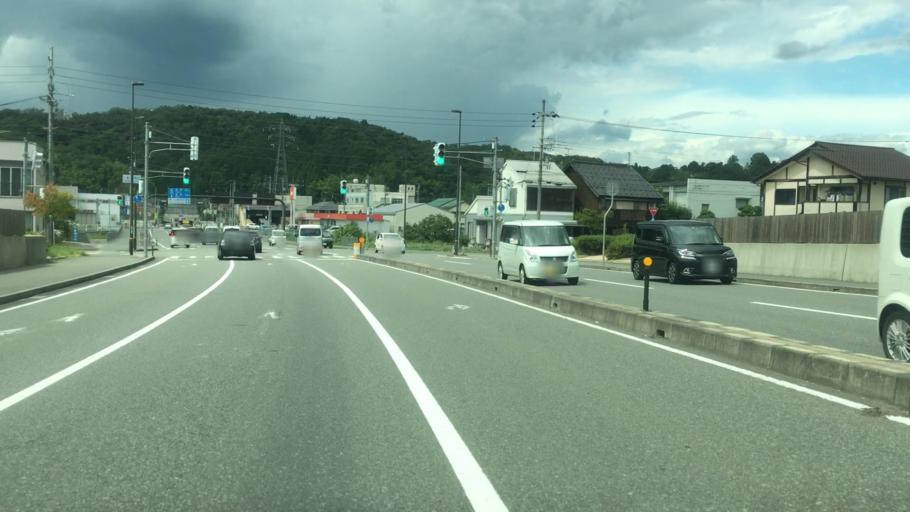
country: JP
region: Hyogo
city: Toyooka
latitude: 35.5282
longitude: 134.8231
